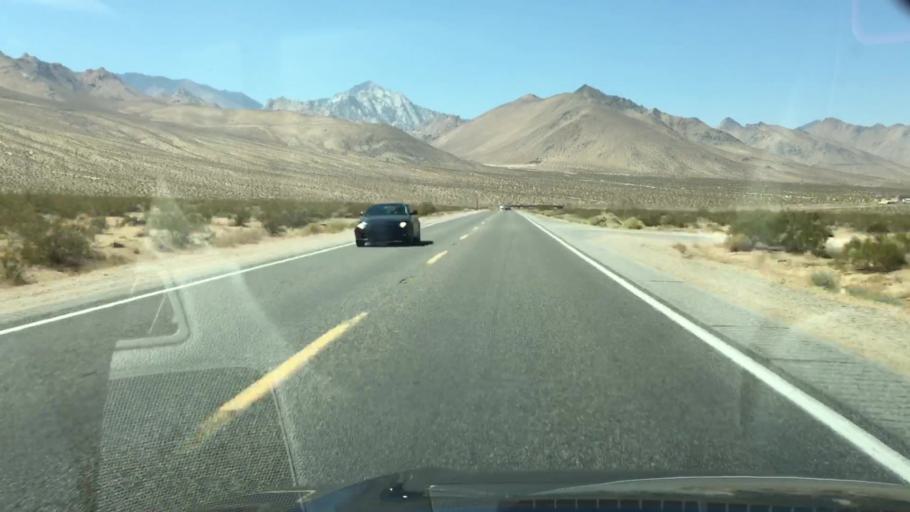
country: US
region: California
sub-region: Kern County
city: Inyokern
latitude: 35.6890
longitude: -117.8571
